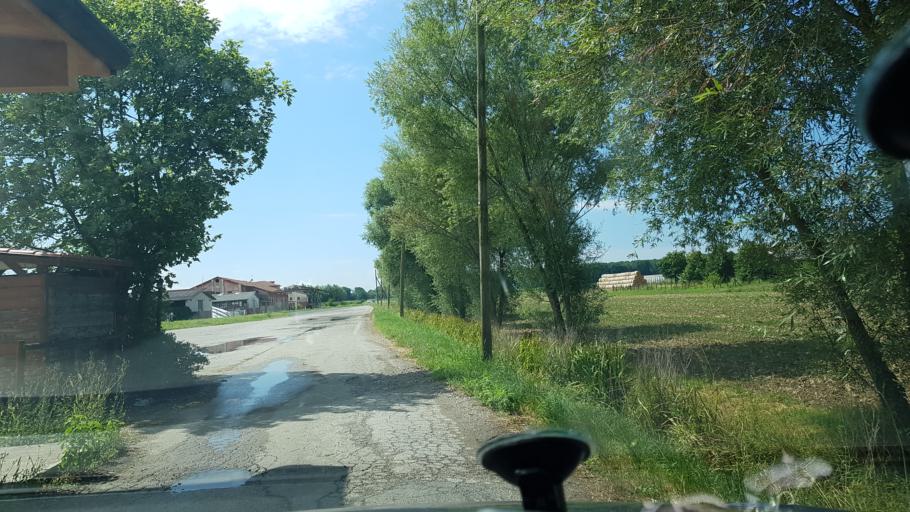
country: IT
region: Friuli Venezia Giulia
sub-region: Provincia di Gorizia
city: San Canzian d'Isonzo
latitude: 45.7812
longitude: 13.4715
